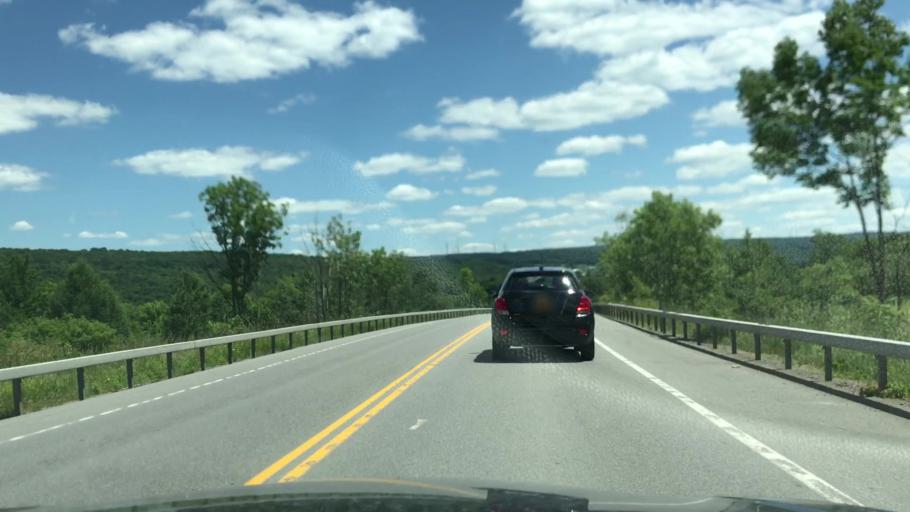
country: US
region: New York
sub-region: Wyoming County
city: Attica
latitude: 42.7683
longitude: -78.3196
